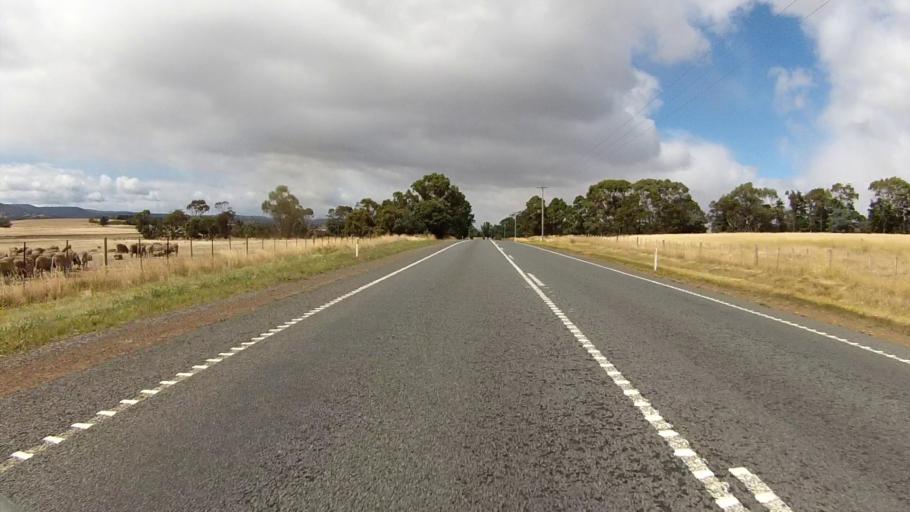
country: AU
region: Tasmania
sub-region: Northern Midlands
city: Evandale
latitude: -41.9806
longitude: 147.5052
